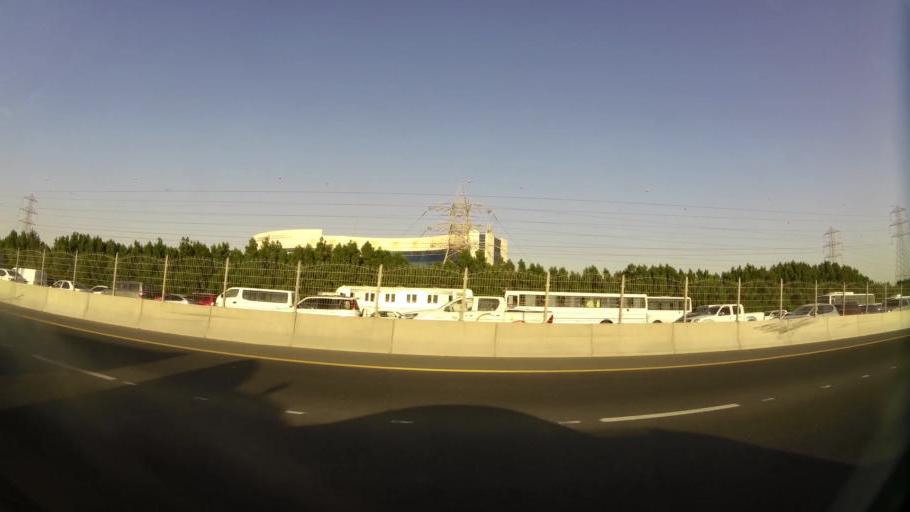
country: AE
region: Ash Shariqah
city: Sharjah
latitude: 25.2567
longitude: 55.4070
